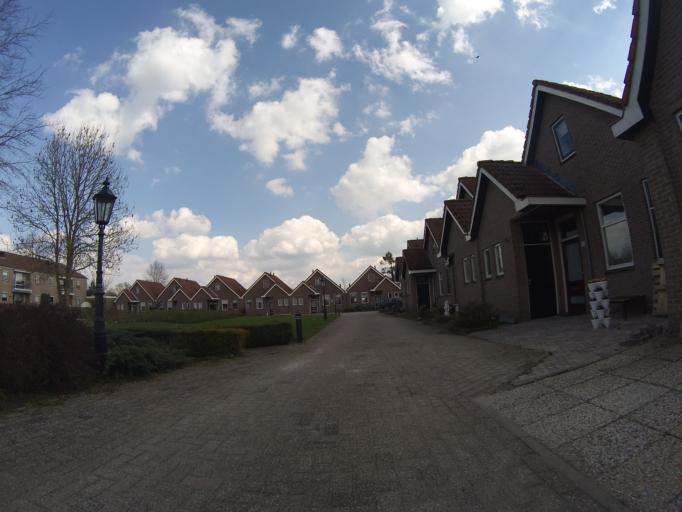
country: NL
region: Gelderland
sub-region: Gemeente Barneveld
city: Terschuur
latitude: 52.1329
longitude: 5.4983
